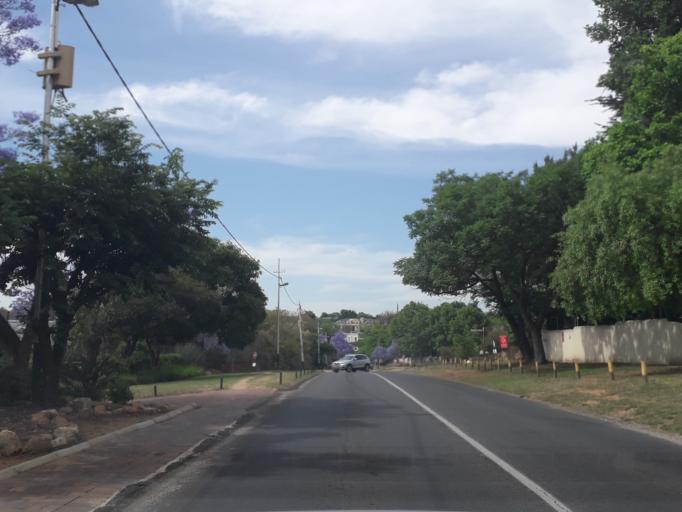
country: ZA
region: Gauteng
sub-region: City of Johannesburg Metropolitan Municipality
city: Diepsloot
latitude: -26.0516
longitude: 28.0163
